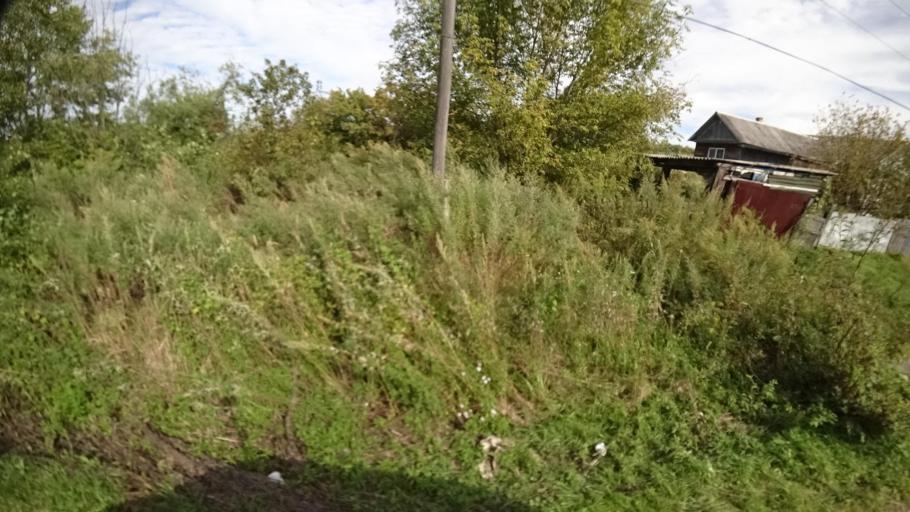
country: RU
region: Primorskiy
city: Dostoyevka
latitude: 44.3269
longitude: 133.4868
